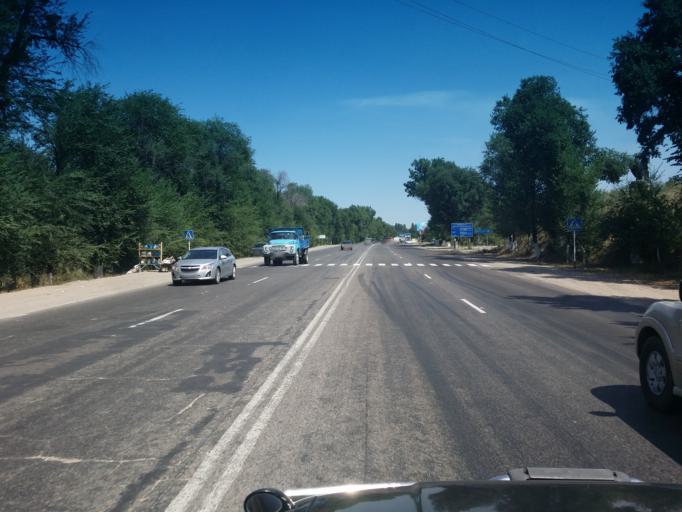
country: KZ
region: Almaty Oblysy
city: Talghar
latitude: 43.4043
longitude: 77.2037
